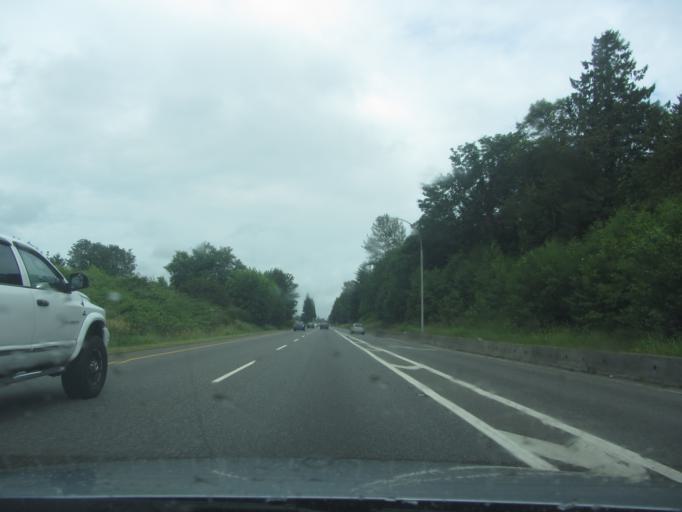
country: CA
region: British Columbia
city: Aldergrove
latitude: 49.0798
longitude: -122.4368
